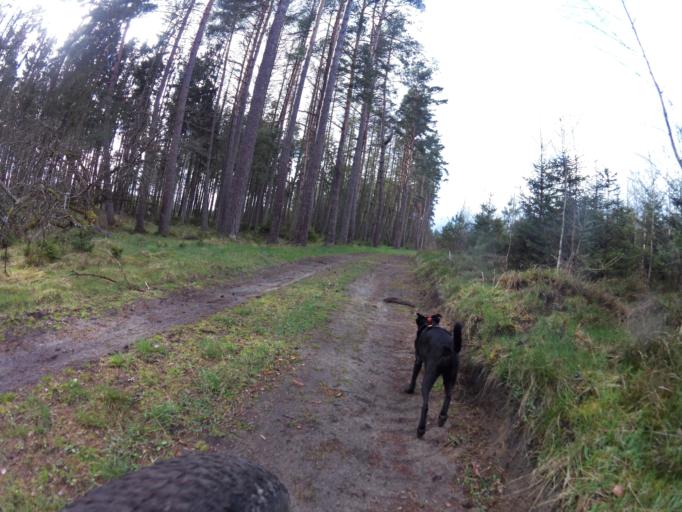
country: PL
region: Pomeranian Voivodeship
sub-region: Powiat slupski
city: Kepice
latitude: 54.2967
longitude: 16.8342
